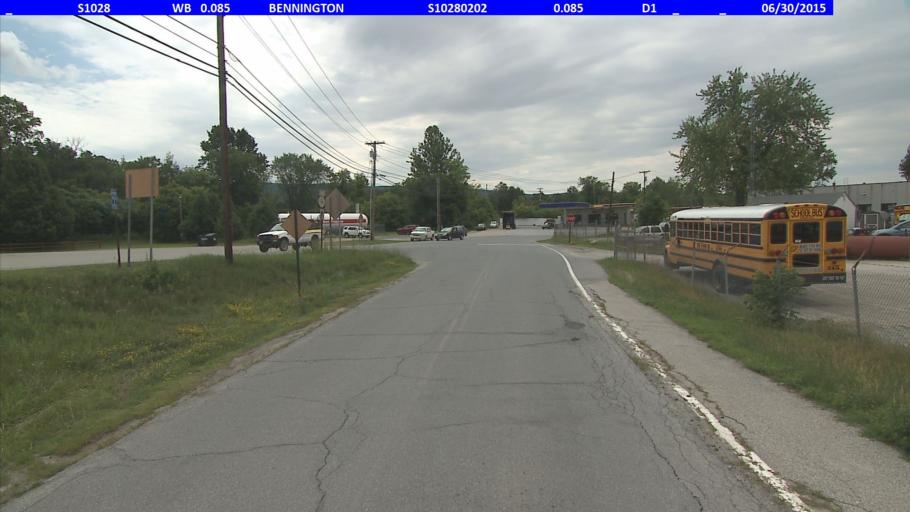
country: US
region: Vermont
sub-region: Bennington County
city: Bennington
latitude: 42.8922
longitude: -73.2019
